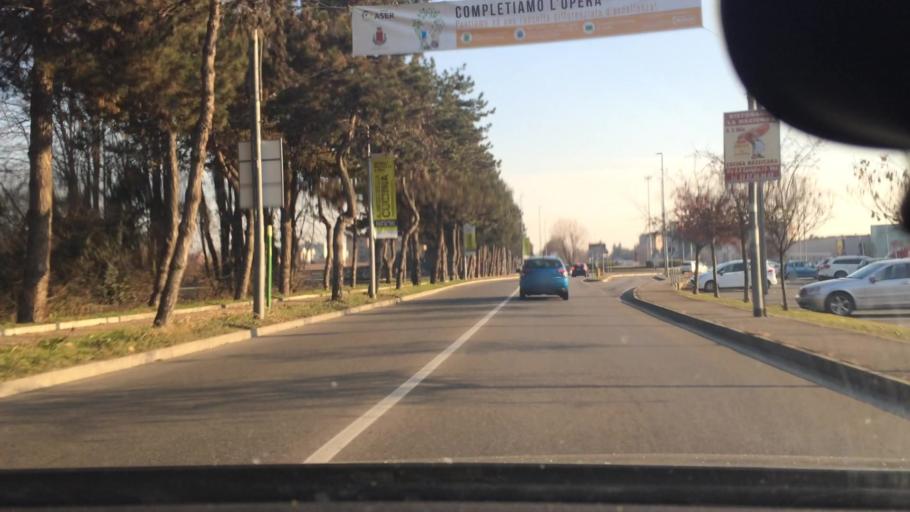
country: IT
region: Lombardy
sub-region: Citta metropolitana di Milano
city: Pogliano Milanese
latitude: 45.5396
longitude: 9.0173
